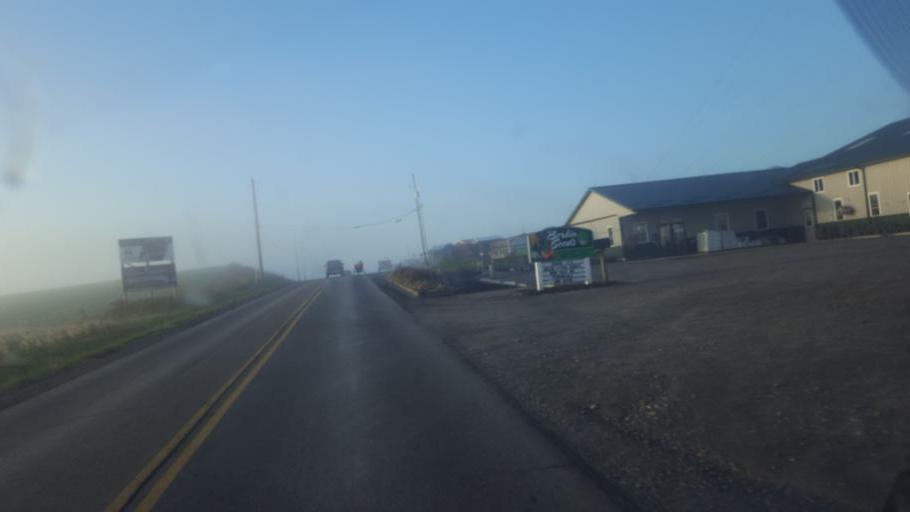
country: US
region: Ohio
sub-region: Holmes County
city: Millersburg
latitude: 40.5563
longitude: -81.7820
